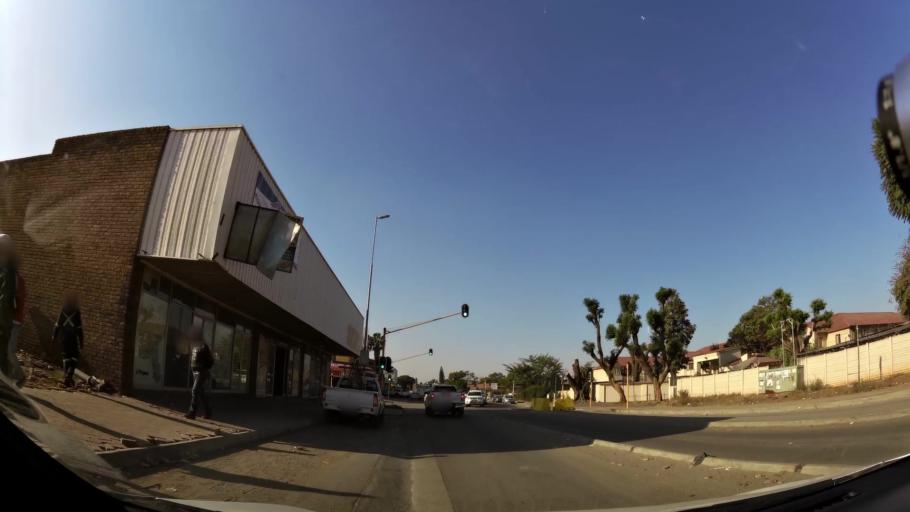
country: ZA
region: North-West
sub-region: Bojanala Platinum District Municipality
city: Rustenburg
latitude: -25.6626
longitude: 27.2459
